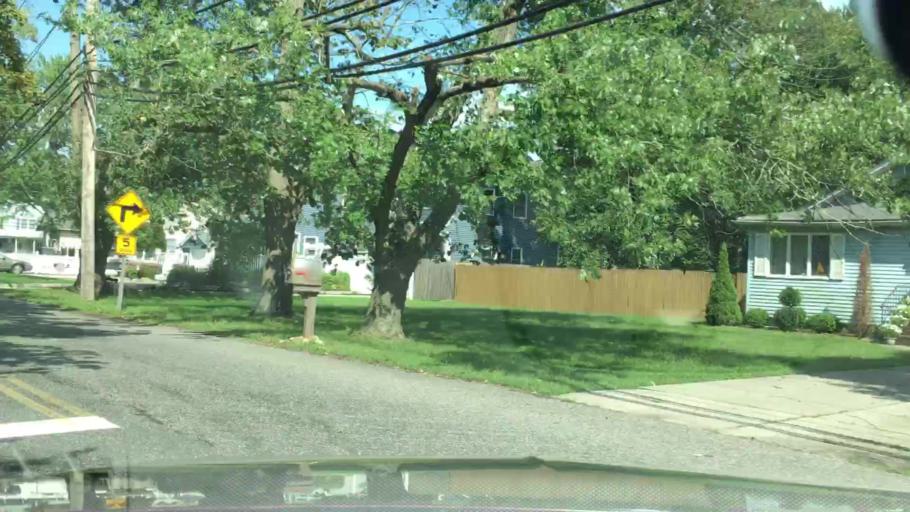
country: US
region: New York
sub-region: Suffolk County
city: Ronkonkoma
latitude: 40.7997
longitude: -73.1264
